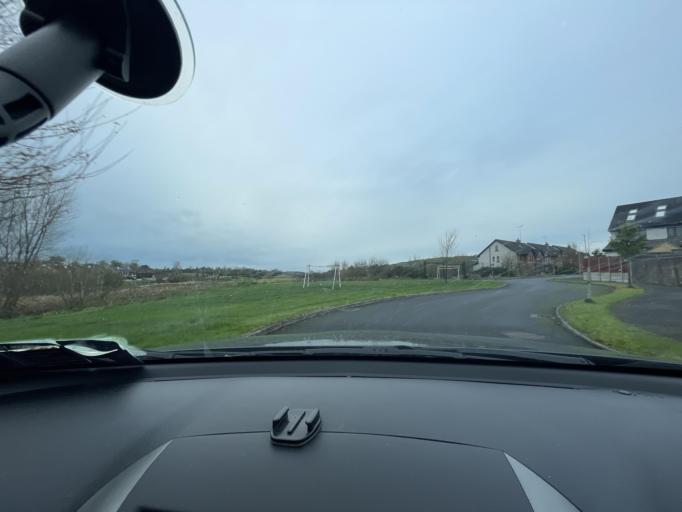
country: IE
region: Ulster
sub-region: An Cabhan
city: Virginia
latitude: 53.8387
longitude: -7.0835
